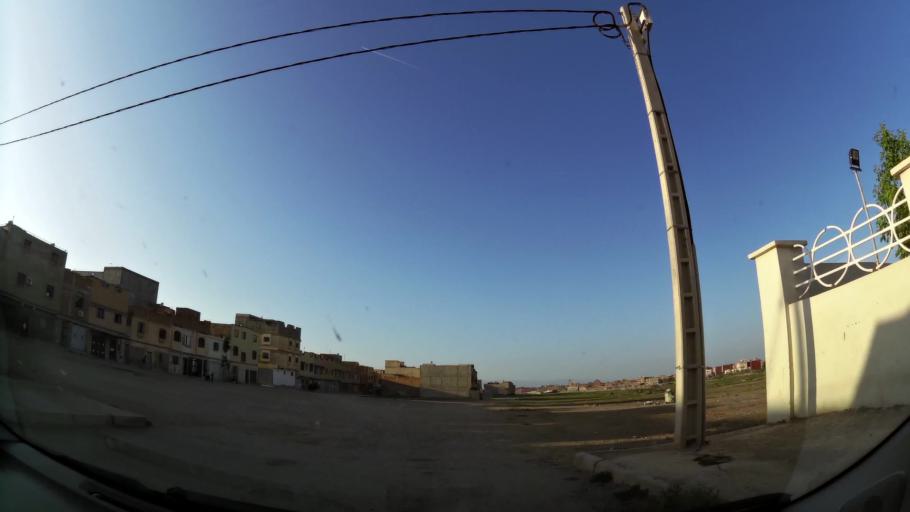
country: MA
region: Oriental
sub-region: Oujda-Angad
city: Oujda
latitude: 34.7063
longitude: -1.9070
